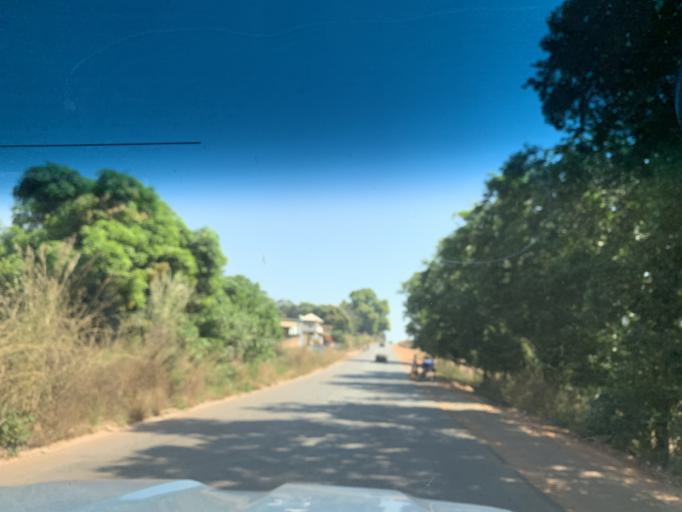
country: GN
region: Kindia
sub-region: Kindia
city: Kindia
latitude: 10.0313
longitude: -12.8691
